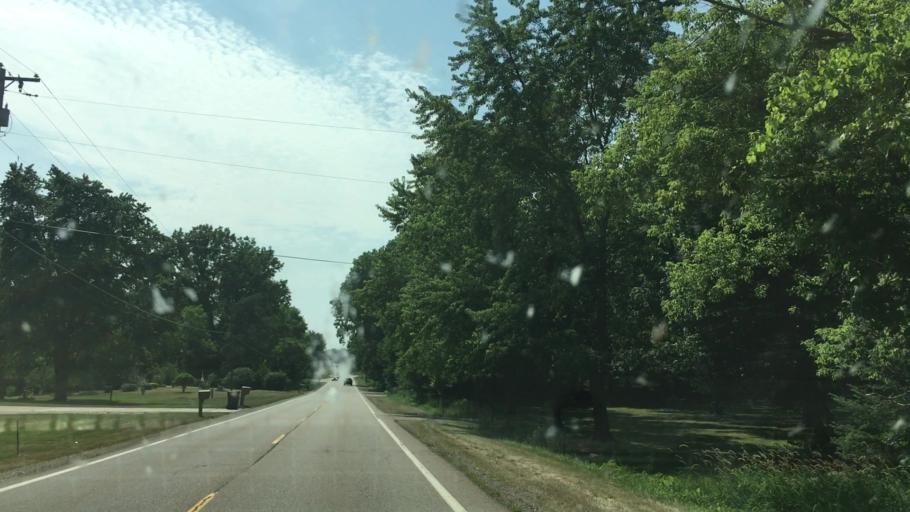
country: US
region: Michigan
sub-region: Kent County
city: Byron Center
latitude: 42.7827
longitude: -85.6780
